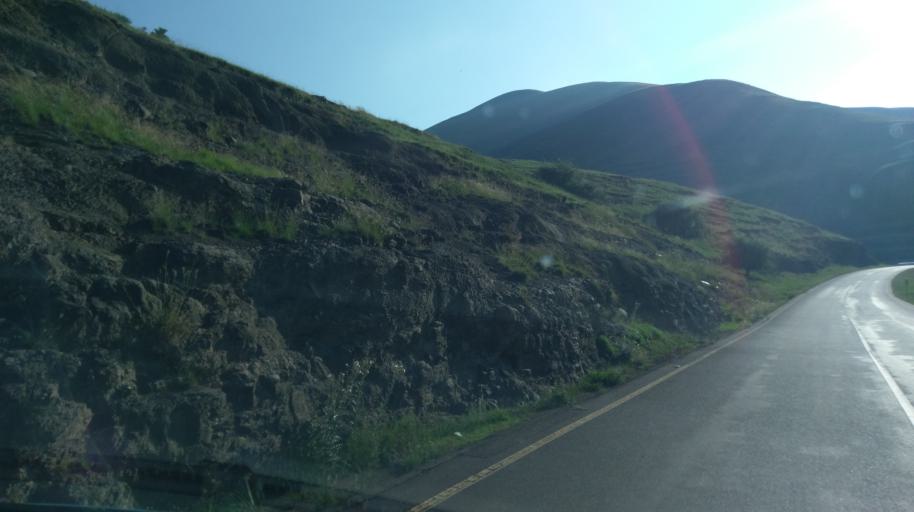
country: LS
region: Butha-Buthe
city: Butha-Buthe
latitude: -29.1127
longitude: 28.4739
